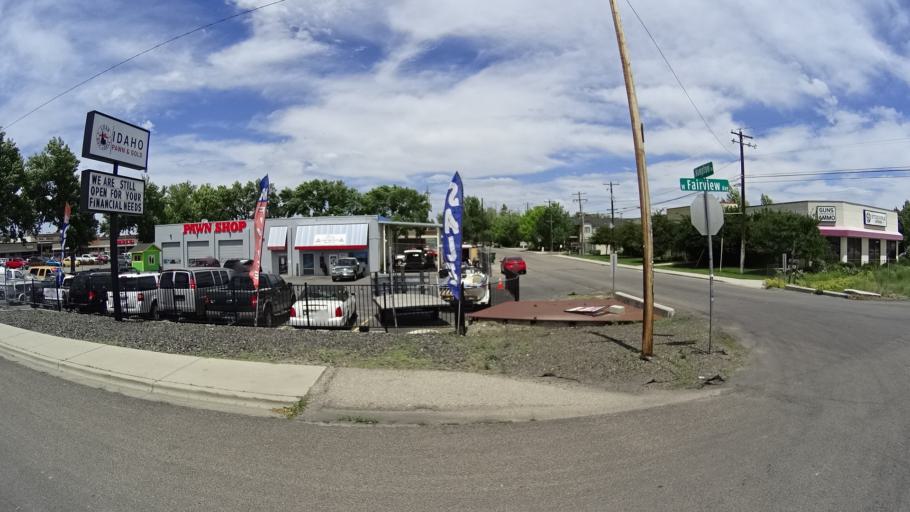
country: US
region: Idaho
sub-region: Ada County
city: Garden City
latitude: 43.6192
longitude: -116.3093
